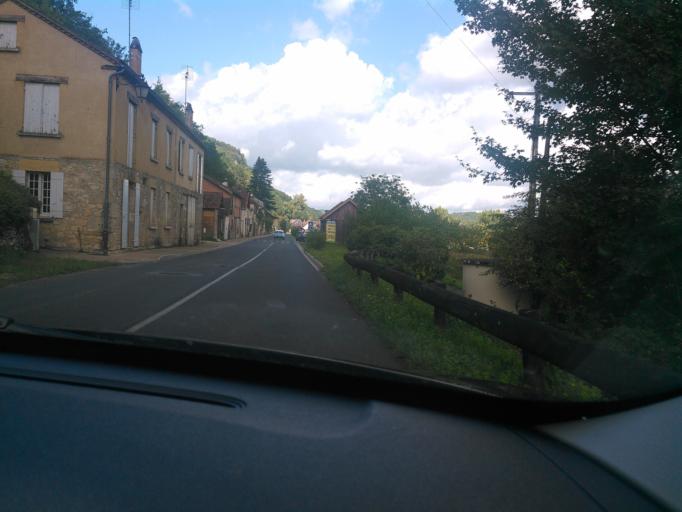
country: FR
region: Aquitaine
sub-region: Departement de la Dordogne
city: Cenac-et-Saint-Julien
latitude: 44.8105
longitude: 1.1532
